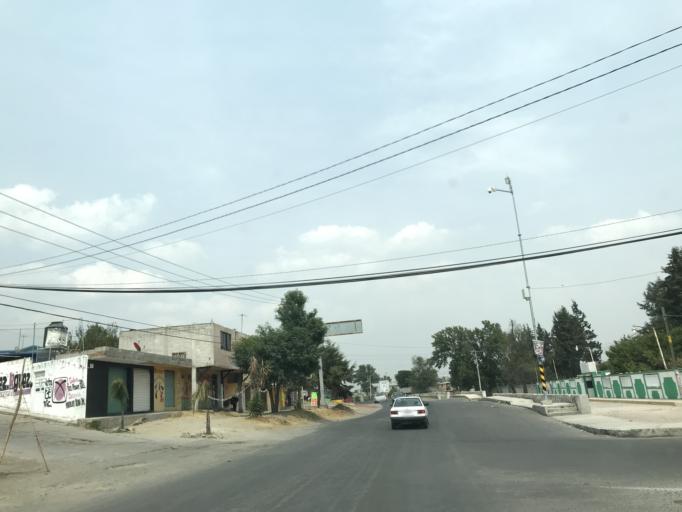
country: MX
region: Tlaxcala
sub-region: Ixtacuixtla de Mariano Matamoros
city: Santa Justina Ecatepec
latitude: 19.3087
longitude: -98.3548
